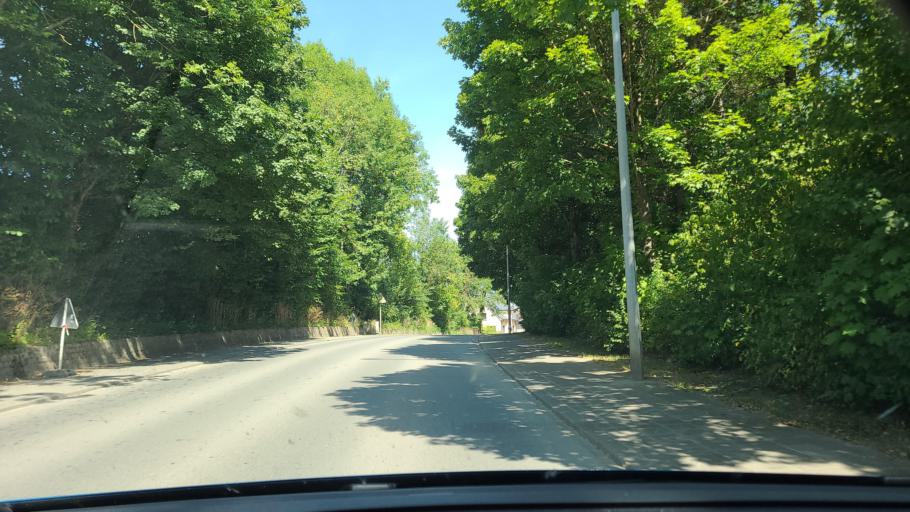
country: LU
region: Luxembourg
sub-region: Canton d'Esch-sur-Alzette
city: Sanem
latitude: 49.5446
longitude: 5.9309
